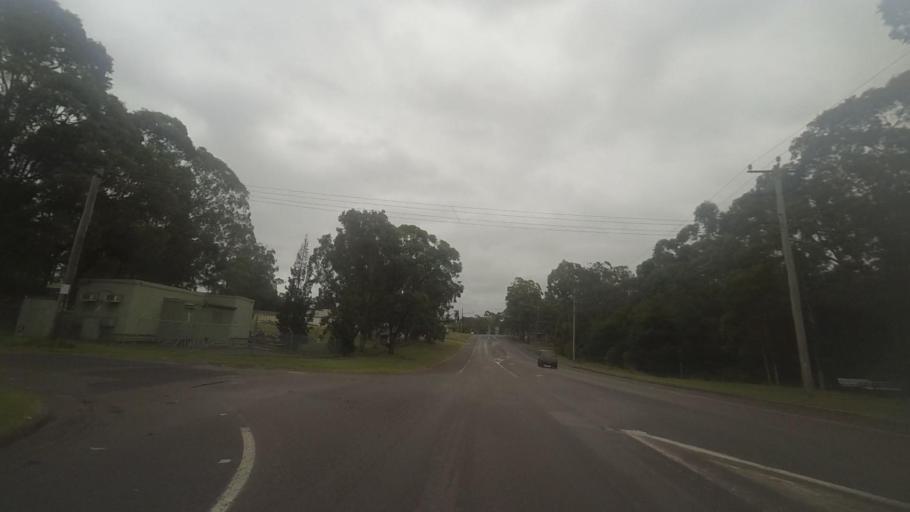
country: AU
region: New South Wales
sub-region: Port Stephens Shire
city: Port Stephens
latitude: -32.6541
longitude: 151.9616
